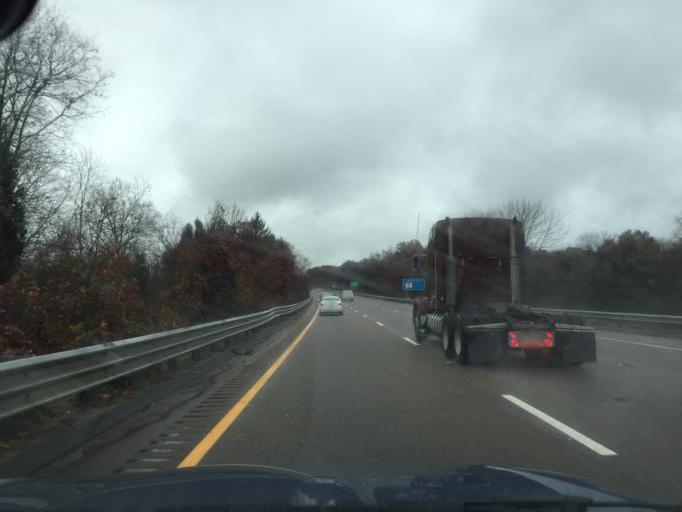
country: US
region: Massachusetts
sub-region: Bristol County
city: North Seekonk
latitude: 41.9107
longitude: -71.3381
